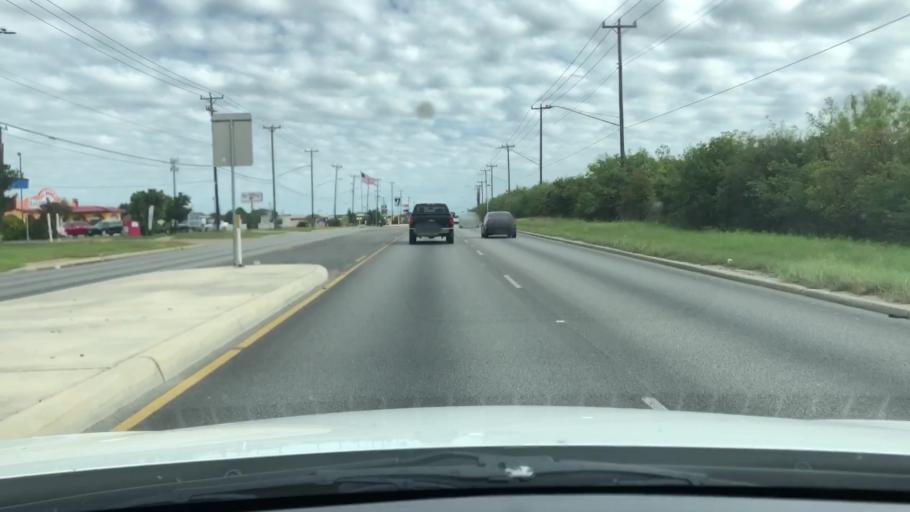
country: US
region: Texas
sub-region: Bexar County
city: Leon Valley
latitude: 29.4902
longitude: -98.6813
